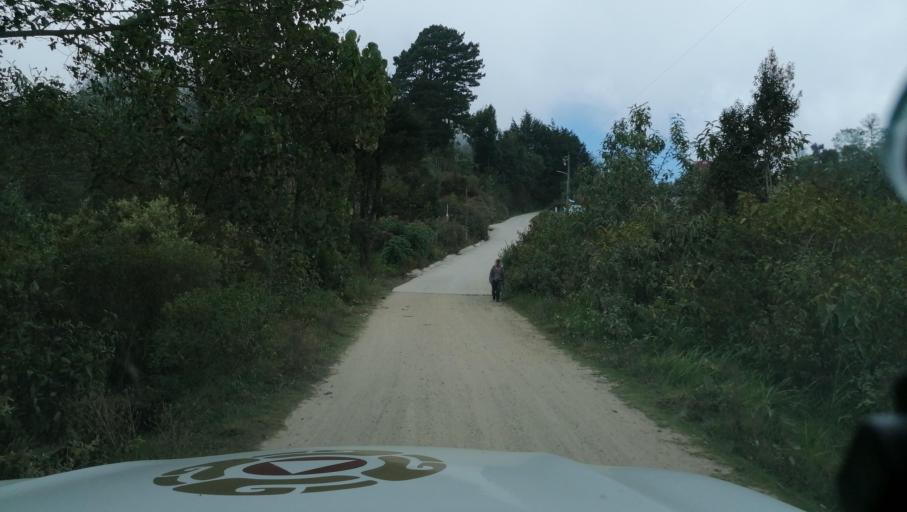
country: MX
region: Chiapas
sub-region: Tapachula
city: Canton Villaflor
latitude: 15.2117
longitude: -92.2401
